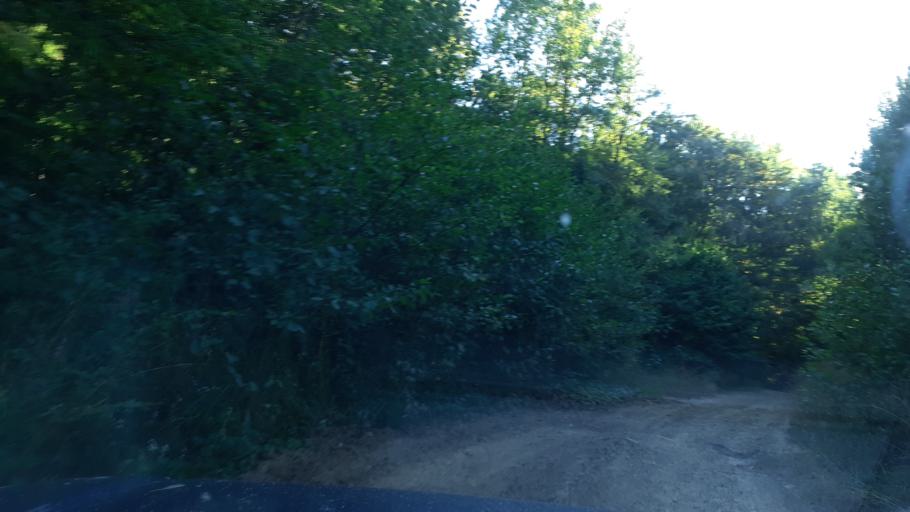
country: RU
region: Krasnodarskiy
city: Pshada
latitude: 44.6564
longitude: 38.4571
